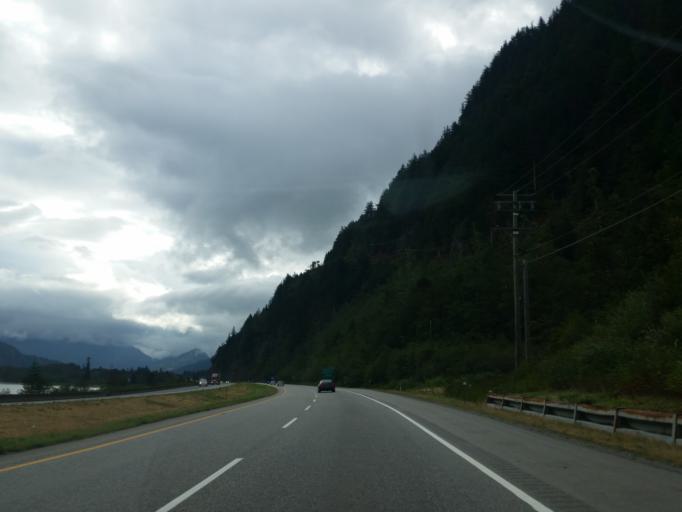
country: CA
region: British Columbia
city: Hope
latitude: 49.3638
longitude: -121.5422
